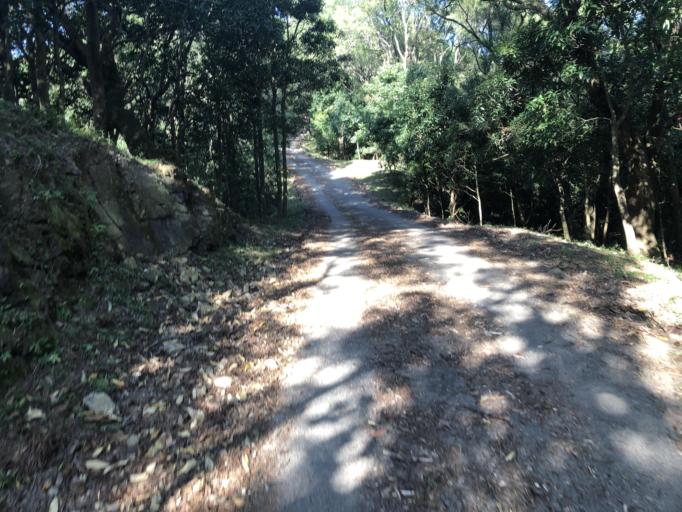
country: HK
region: Tsuen Wan
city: Tsuen Wan
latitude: 22.3963
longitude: 114.0880
